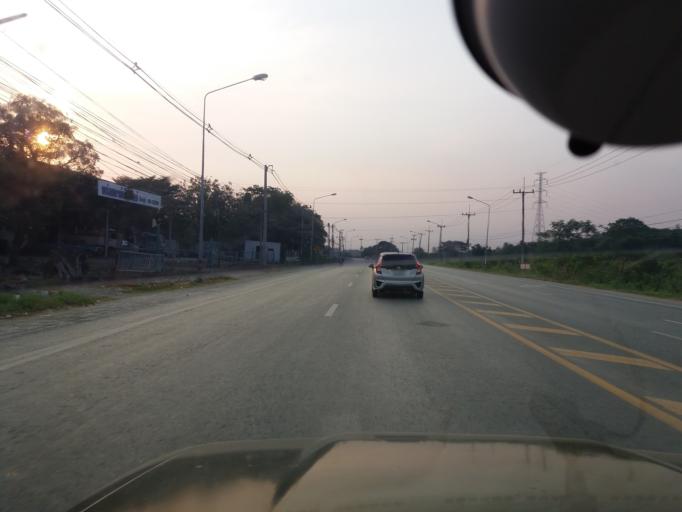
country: TH
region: Sing Buri
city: Sing Buri
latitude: 14.8855
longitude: 100.3846
